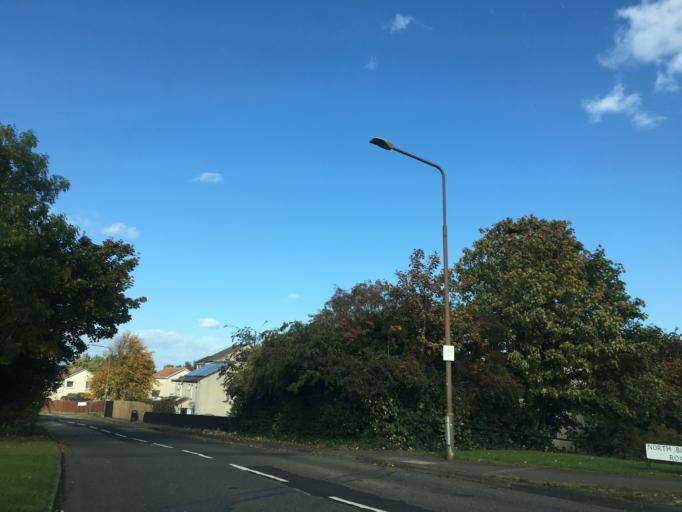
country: GB
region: Scotland
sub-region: Edinburgh
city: Currie
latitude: 55.9530
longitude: -3.3055
